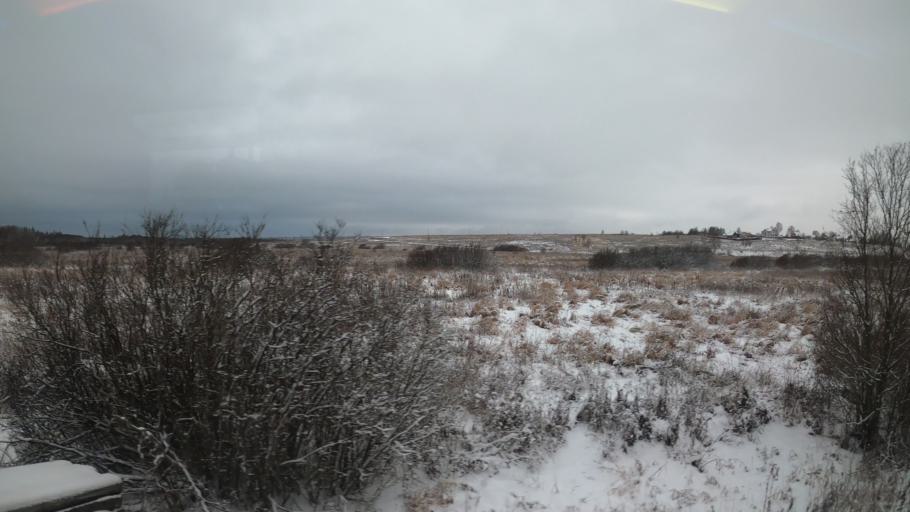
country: RU
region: Jaroslavl
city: Pereslavl'-Zalesskiy
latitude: 56.6977
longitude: 38.9165
